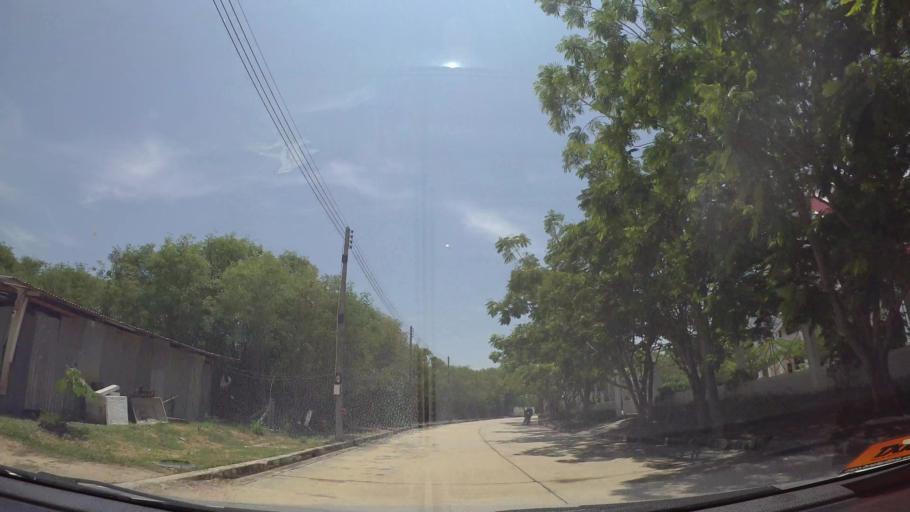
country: TH
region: Chon Buri
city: Chon Buri
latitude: 13.3400
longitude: 100.9438
